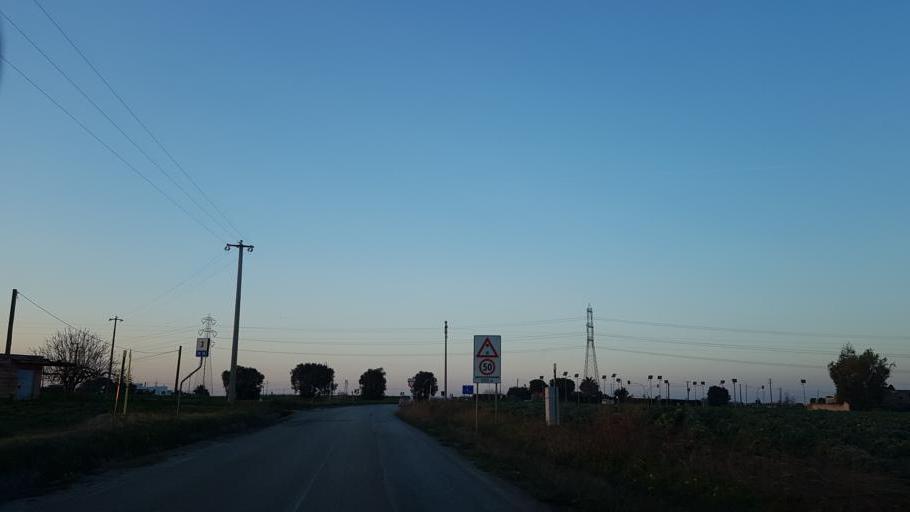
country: IT
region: Apulia
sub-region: Provincia di Brindisi
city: La Rosa
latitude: 40.5889
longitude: 17.9443
